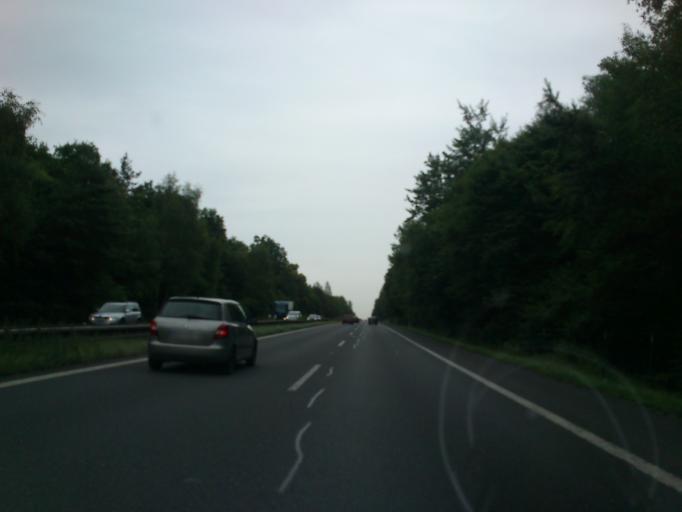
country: CZ
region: Central Bohemia
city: Celakovice
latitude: 50.2309
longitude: 14.7279
